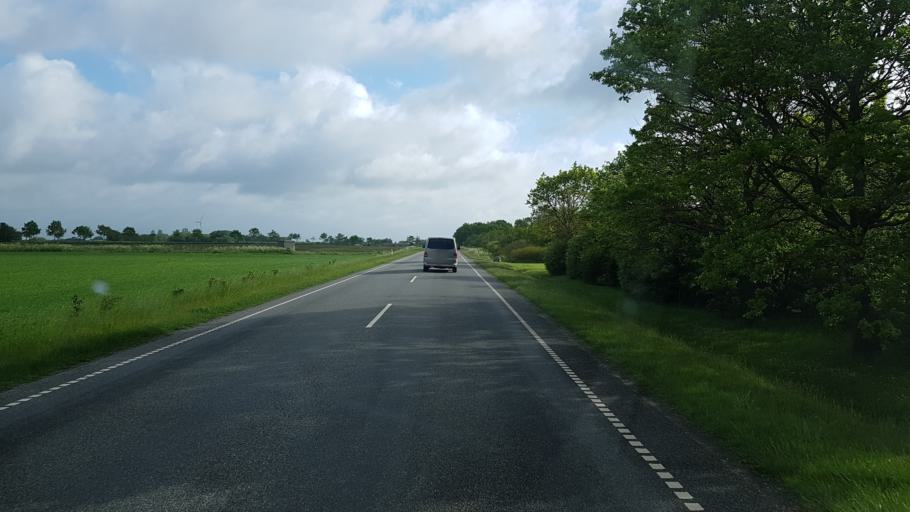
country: DK
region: South Denmark
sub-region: Vejen Kommune
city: Vejen
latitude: 55.4142
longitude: 9.1352
